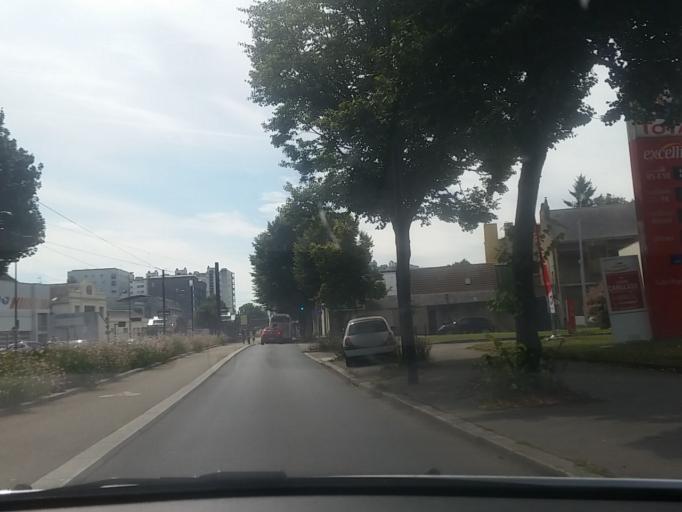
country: FR
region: Pays de la Loire
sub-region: Departement de la Loire-Atlantique
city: Nantes
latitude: 47.2047
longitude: -1.5471
